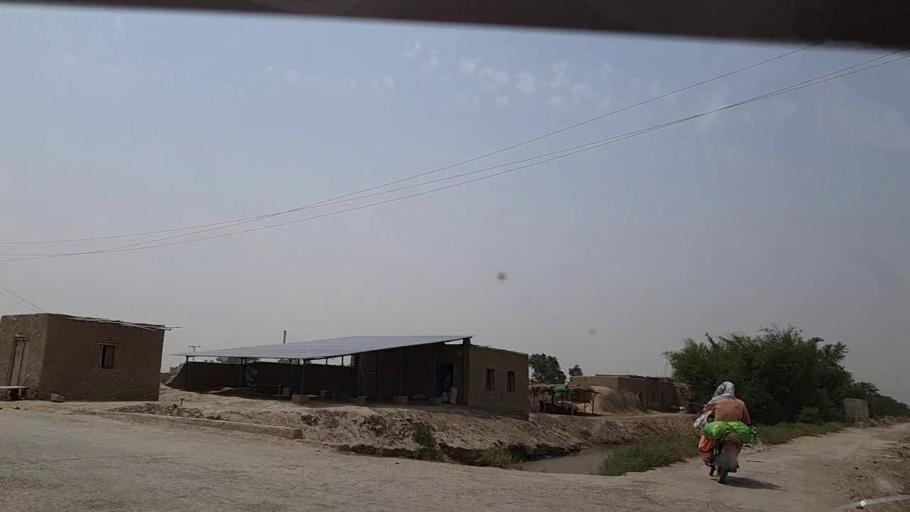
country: PK
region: Sindh
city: Khairpur Nathan Shah
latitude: 27.0215
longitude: 67.5831
